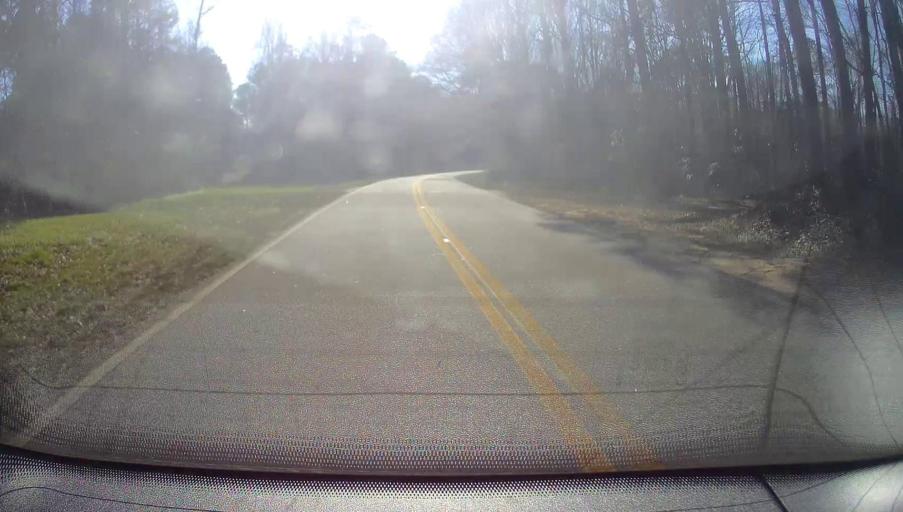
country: US
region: Georgia
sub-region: Monroe County
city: Forsyth
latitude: 33.0601
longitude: -83.8681
